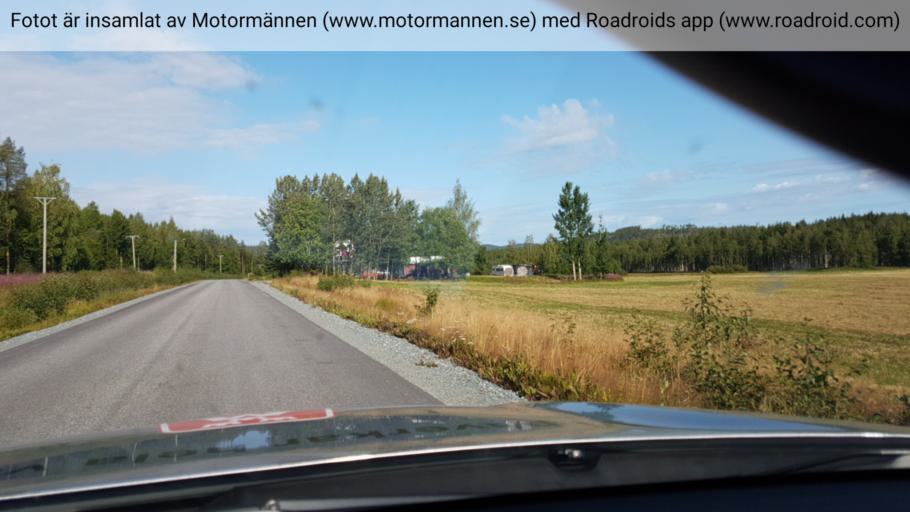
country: SE
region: Norrbotten
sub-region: Alvsbyns Kommun
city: AElvsbyn
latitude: 65.6387
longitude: 20.8945
